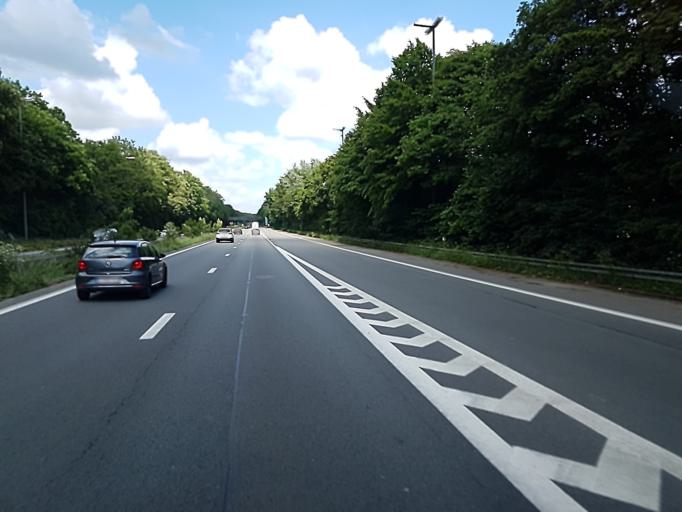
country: BE
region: Wallonia
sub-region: Province du Brabant Wallon
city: Braine-l'Alleud
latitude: 50.6712
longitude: 4.3912
